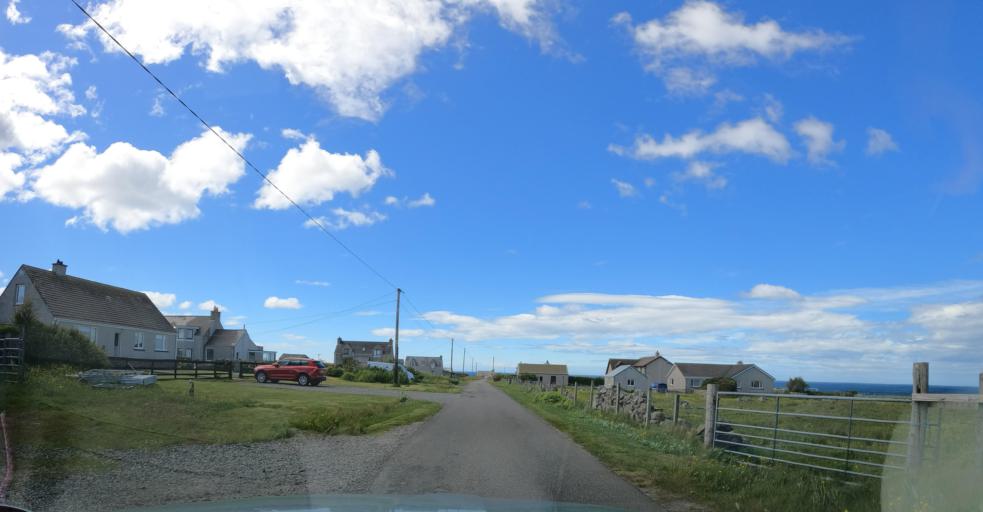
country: GB
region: Scotland
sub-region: Eilean Siar
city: Isle of Lewis
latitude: 58.3580
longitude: -6.5583
